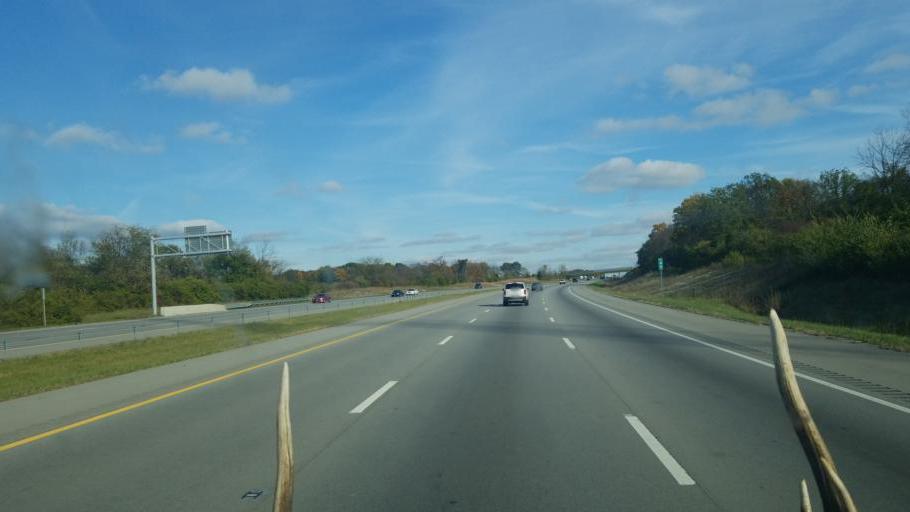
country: US
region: Ohio
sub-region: Clark County
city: Enon
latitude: 39.8934
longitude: -83.9152
